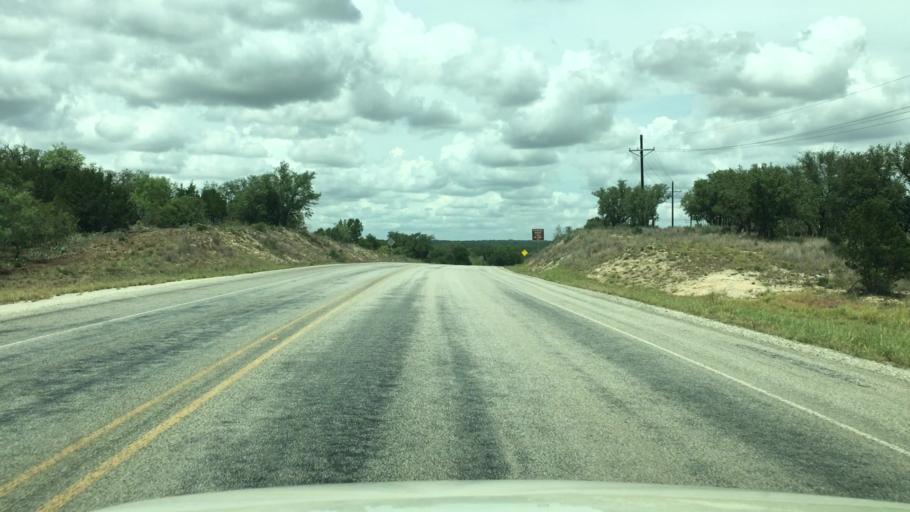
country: US
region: Texas
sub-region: McCulloch County
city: Brady
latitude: 31.0093
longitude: -99.2065
